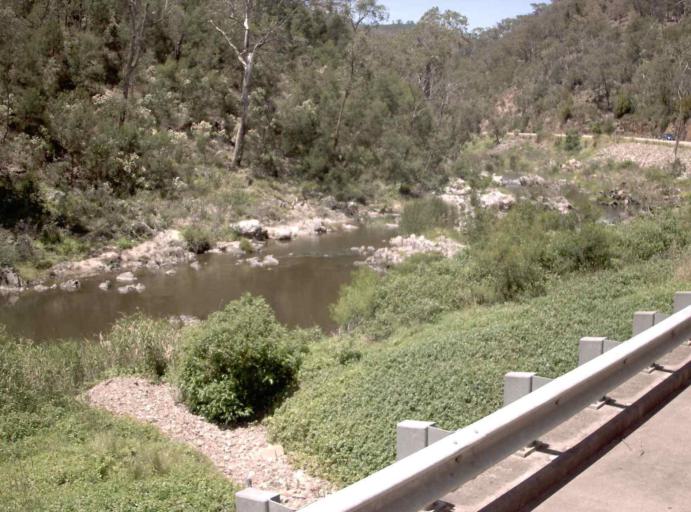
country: AU
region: Victoria
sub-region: East Gippsland
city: Bairnsdale
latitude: -37.4294
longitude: 147.8326
